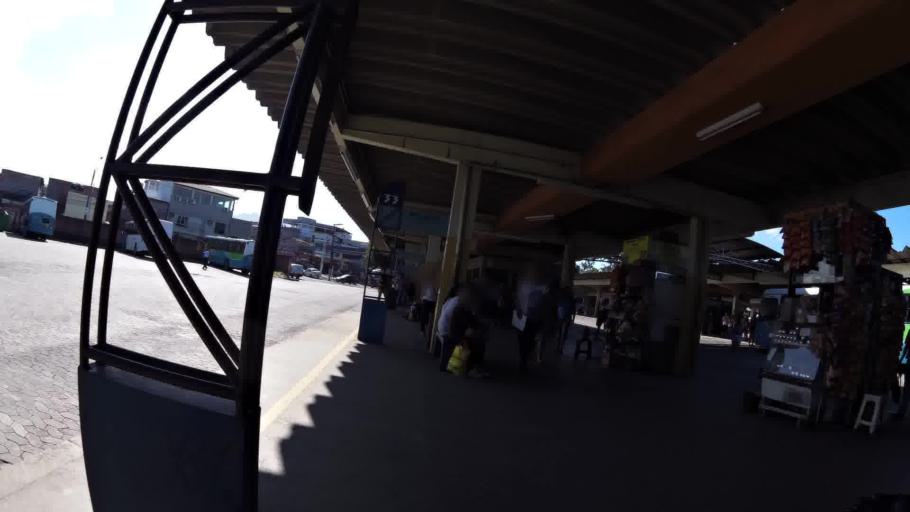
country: BR
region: Espirito Santo
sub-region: Vila Velha
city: Vila Velha
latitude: -20.2310
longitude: -40.2702
